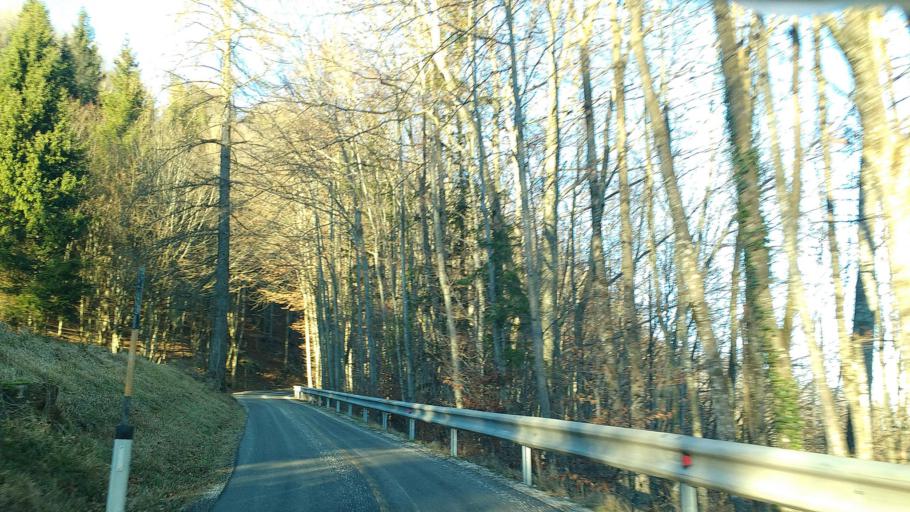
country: AT
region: Upper Austria
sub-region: Politischer Bezirk Kirchdorf an der Krems
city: Micheldorf in Oberoesterreich
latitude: 47.8947
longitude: 14.2170
